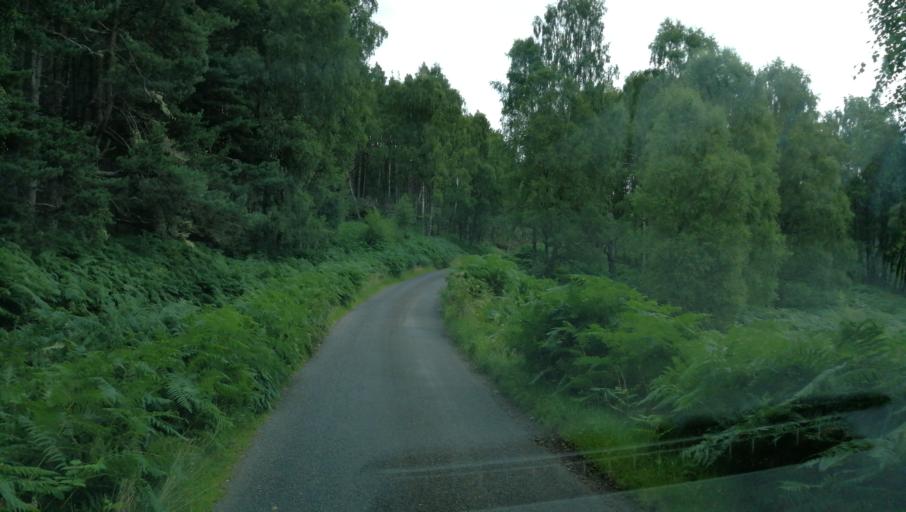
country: GB
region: Scotland
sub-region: Highland
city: Beauly
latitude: 57.3168
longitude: -4.8224
